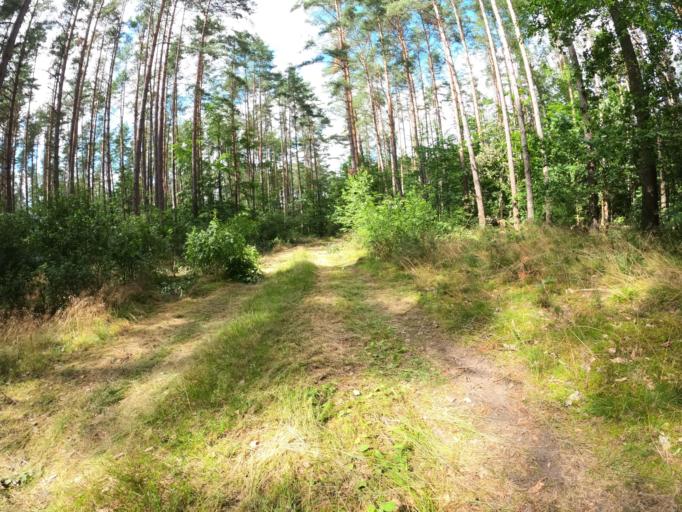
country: PL
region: West Pomeranian Voivodeship
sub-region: Powiat bialogardzki
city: Tychowo
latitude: 54.0115
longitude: 16.3554
